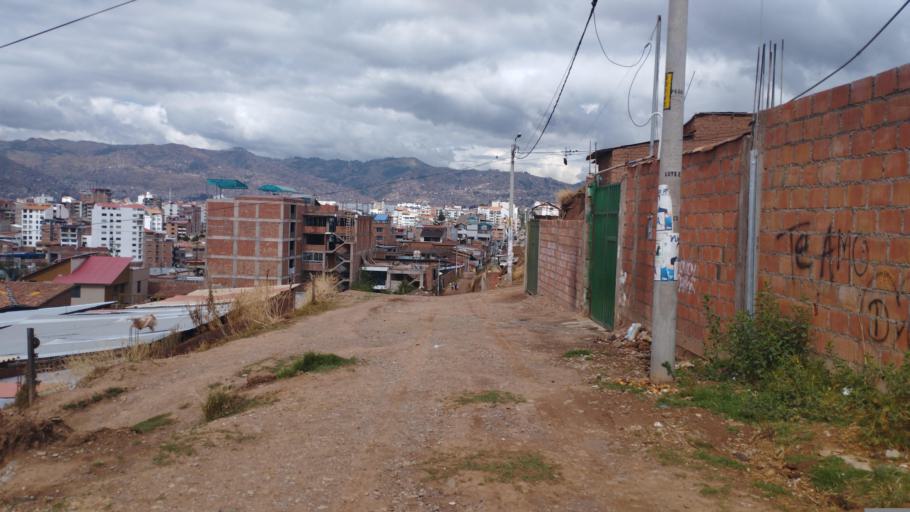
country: PE
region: Cusco
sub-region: Provincia de Cusco
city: Cusco
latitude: -13.5239
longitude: -71.9404
